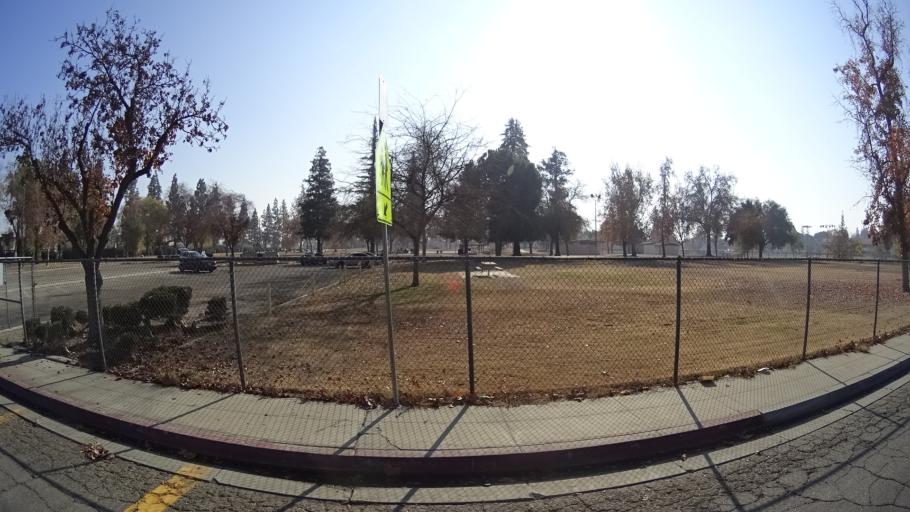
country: US
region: California
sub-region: Kern County
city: Bakersfield
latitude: 35.3419
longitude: -119.0588
